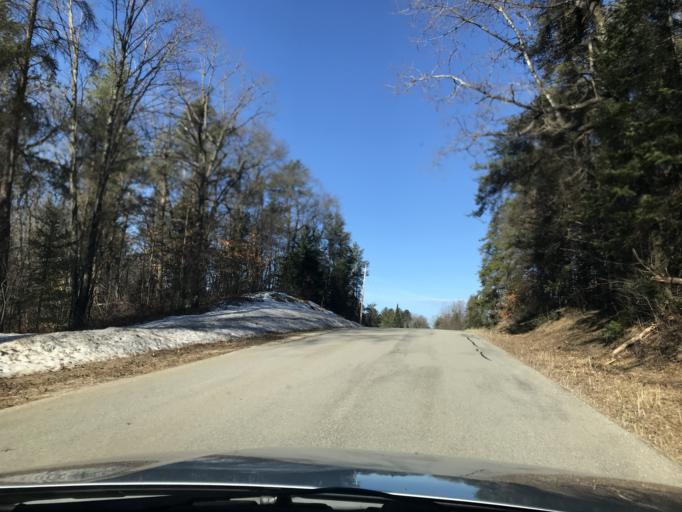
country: US
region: Wisconsin
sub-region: Marinette County
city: Niagara
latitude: 45.3900
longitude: -88.0630
